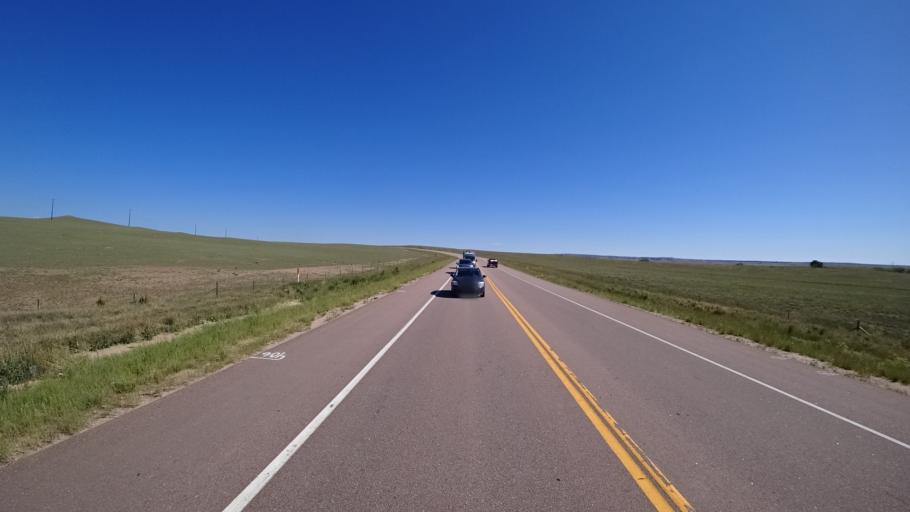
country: US
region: Colorado
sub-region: El Paso County
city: Security-Widefield
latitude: 38.7890
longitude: -104.6582
